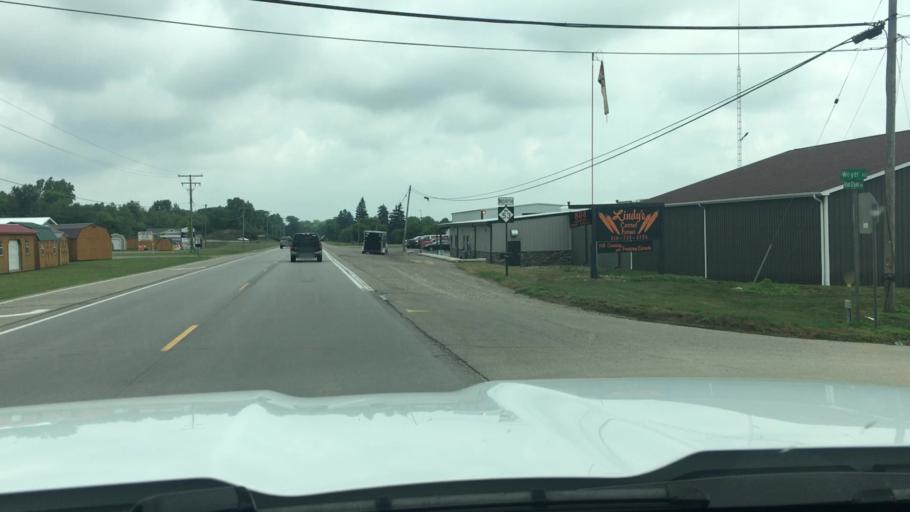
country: US
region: Michigan
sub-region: Lapeer County
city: Imlay City
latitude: 43.0507
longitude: -83.0720
